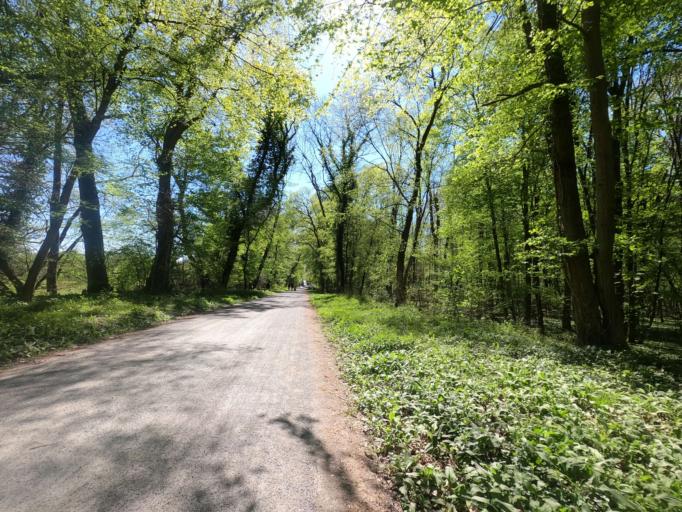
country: DE
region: Hesse
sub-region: Regierungsbezirk Darmstadt
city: Gross-Gerau
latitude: 49.9451
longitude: 8.4993
